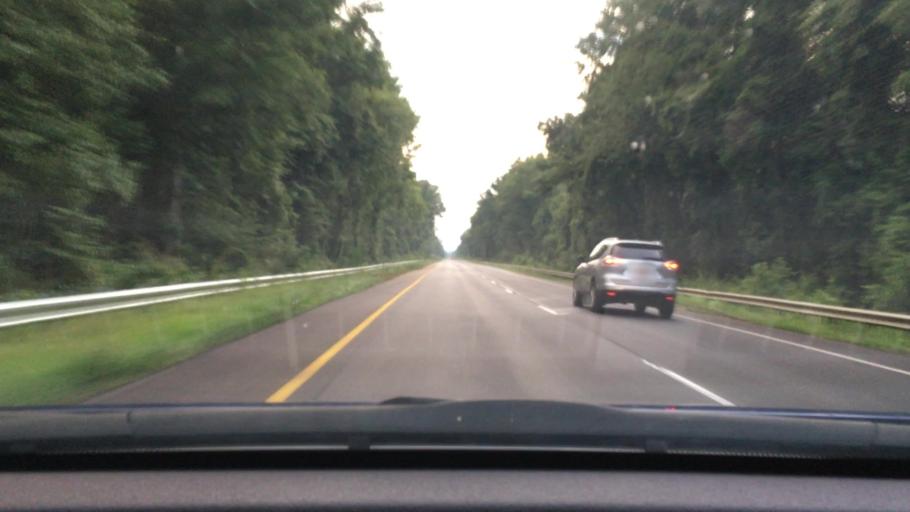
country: US
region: South Carolina
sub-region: Sumter County
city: Stateburg
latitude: 33.9525
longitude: -80.5793
